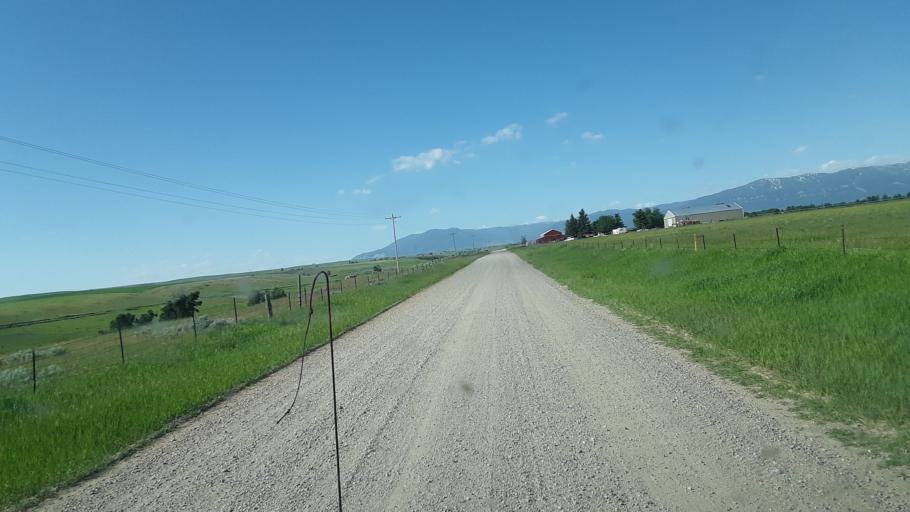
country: US
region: Montana
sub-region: Carbon County
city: Red Lodge
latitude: 45.3388
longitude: -109.1613
